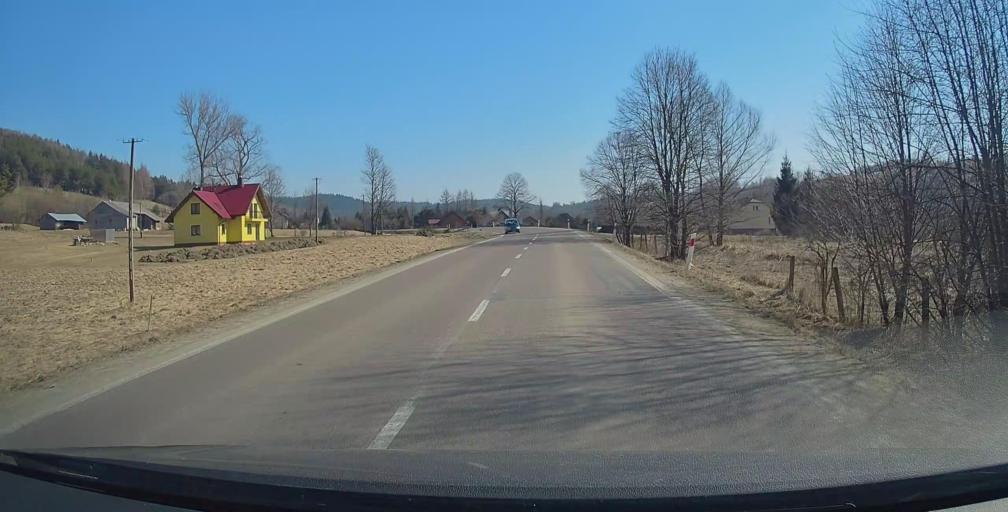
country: PL
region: Subcarpathian Voivodeship
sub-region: Powiat przemyski
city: Bircza
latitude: 49.5788
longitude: 22.5404
